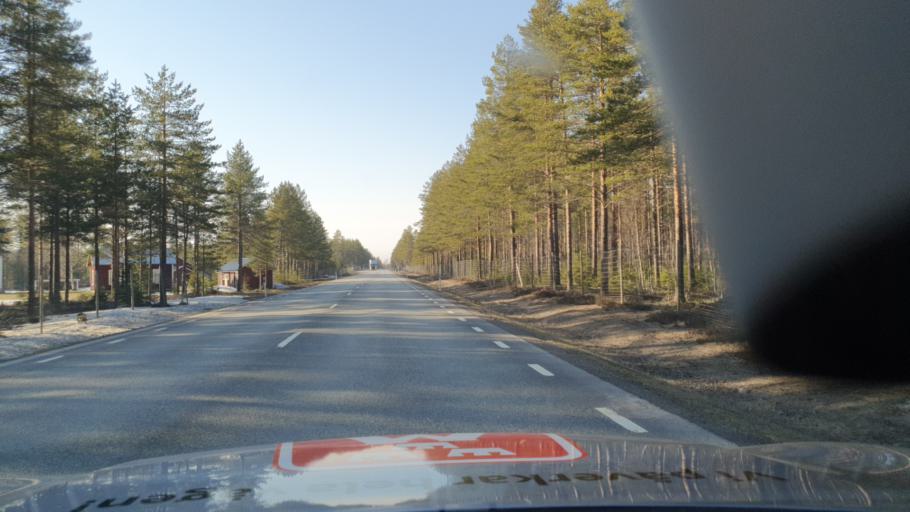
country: SE
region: Vaesterbotten
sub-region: Skelleftea Kommun
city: Burea
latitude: 64.5605
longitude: 21.2357
